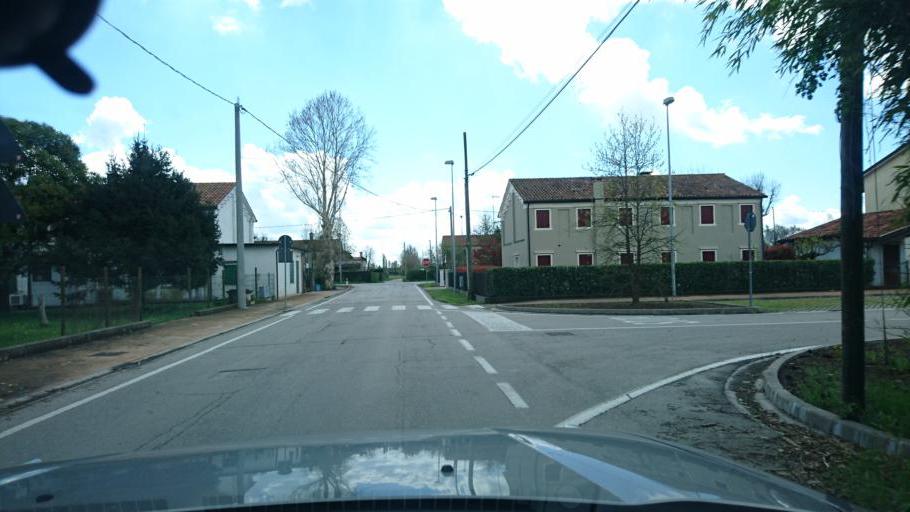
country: IT
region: Veneto
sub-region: Provincia di Padova
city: Piazzola sul Brenta
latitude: 45.5405
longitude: 11.7688
